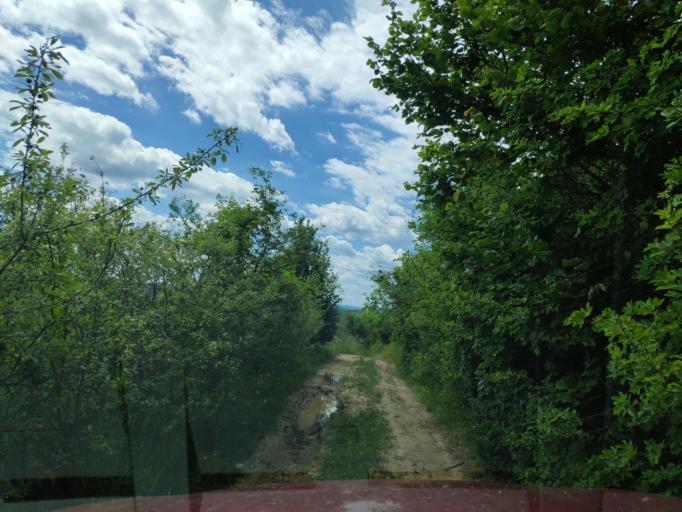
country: HU
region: Borsod-Abauj-Zemplen
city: Ozd
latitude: 48.2764
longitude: 20.2254
